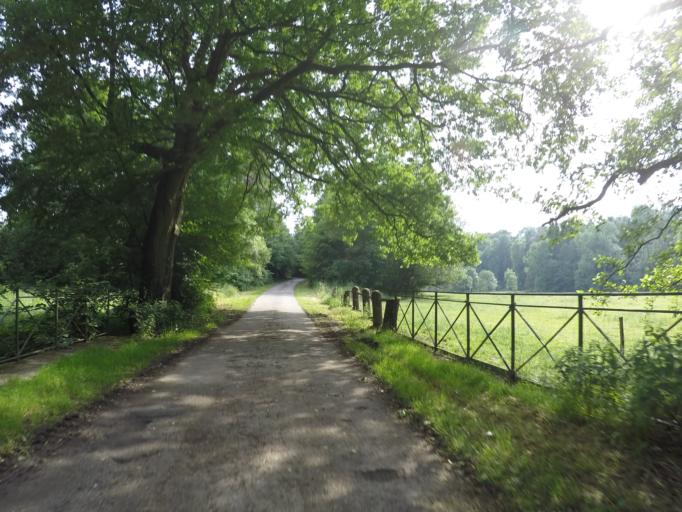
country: BE
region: Wallonia
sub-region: Province de Namur
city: Assesse
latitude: 50.3298
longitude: 5.0489
